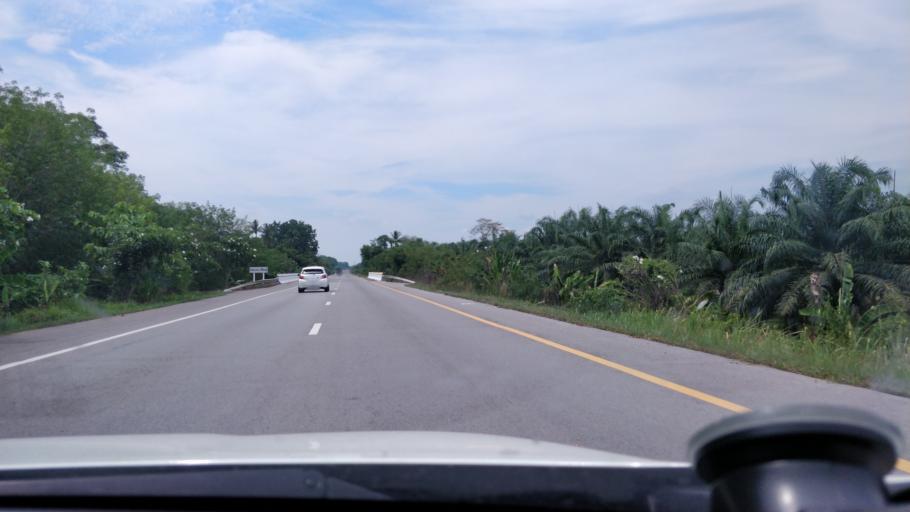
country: TH
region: Surat Thani
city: Khian Sa
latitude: 8.7794
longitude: 99.1614
